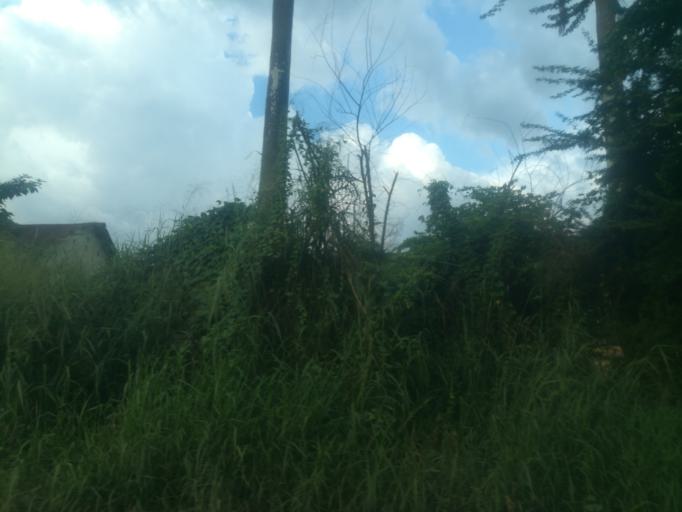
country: NG
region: Oyo
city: Ibadan
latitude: 7.3806
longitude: 3.8415
